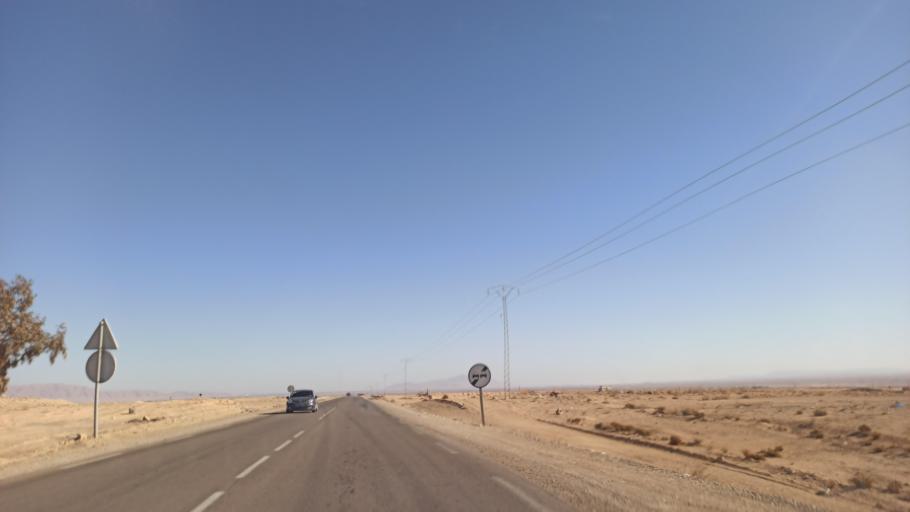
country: TN
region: Gafsa
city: Al Metlaoui
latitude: 34.3143
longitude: 8.4962
